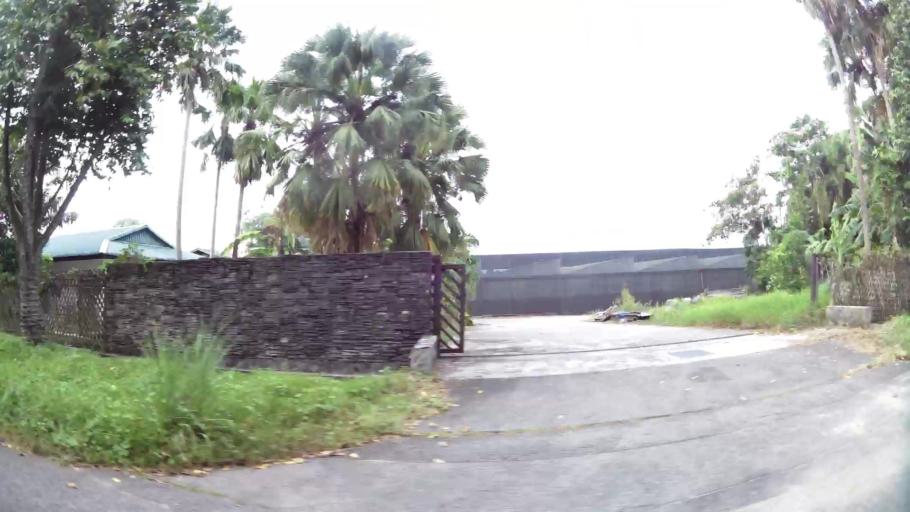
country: MY
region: Johor
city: Johor Bahru
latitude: 1.4423
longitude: 103.7104
